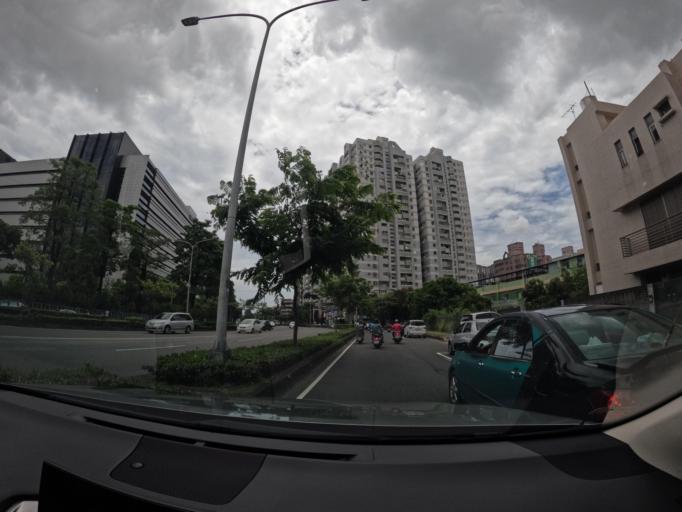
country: TW
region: Kaohsiung
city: Kaohsiung
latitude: 22.7253
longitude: 120.3020
